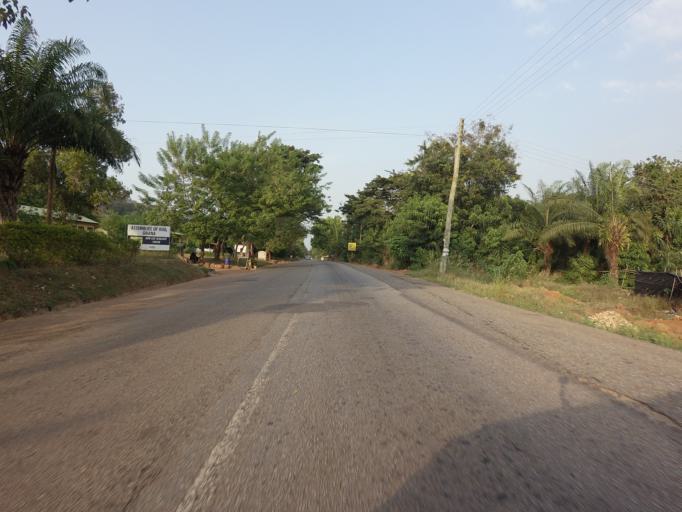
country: GH
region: Volta
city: Ho
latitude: 6.5467
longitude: 0.2913
